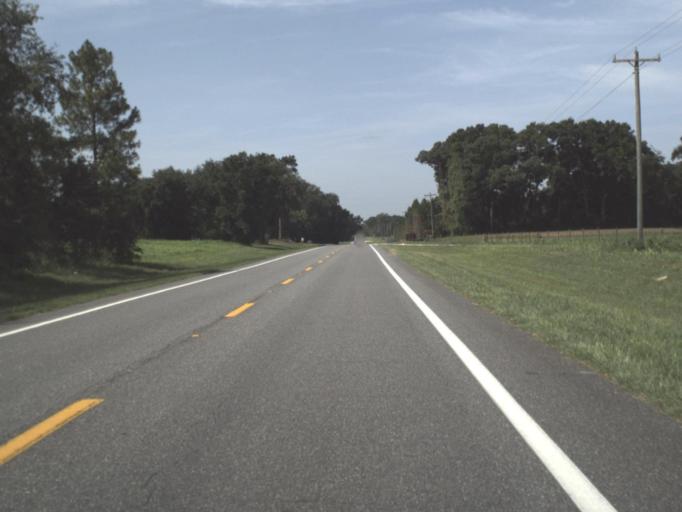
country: US
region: Florida
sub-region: Lafayette County
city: Mayo
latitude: 30.1495
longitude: -83.1634
